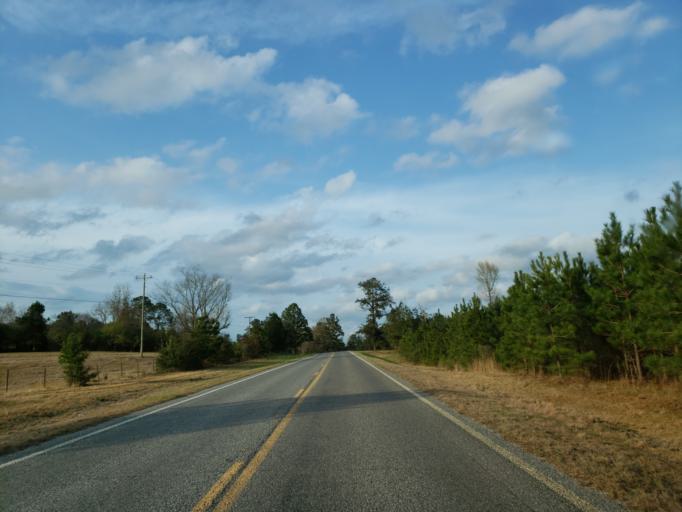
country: US
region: Mississippi
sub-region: Clarke County
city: Stonewall
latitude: 32.1778
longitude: -88.6777
